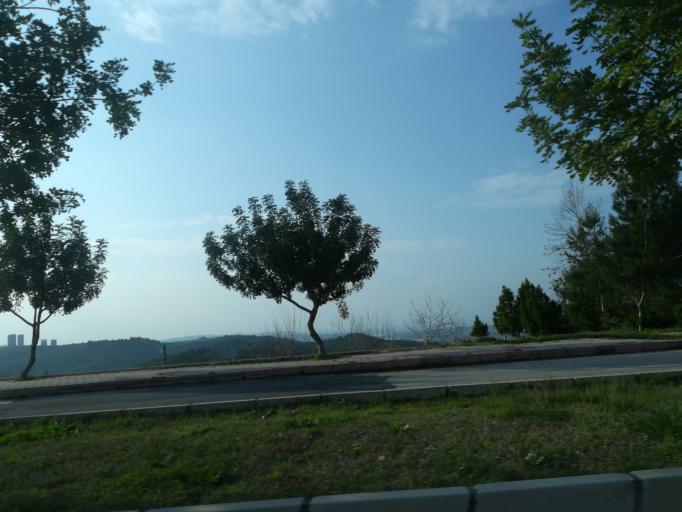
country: TR
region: Adana
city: Adana
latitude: 37.0715
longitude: 35.3805
